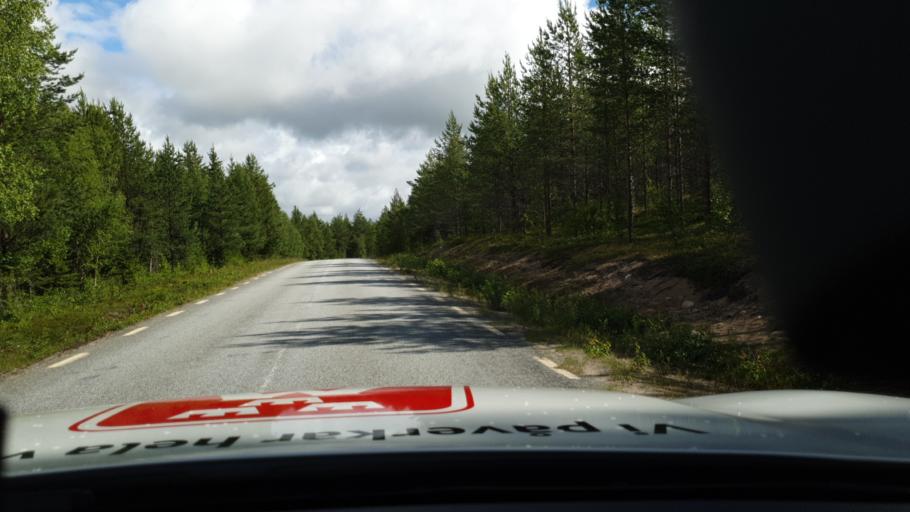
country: SE
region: Norrbotten
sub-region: Pitea Kommun
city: Rosvik
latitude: 65.4340
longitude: 21.8636
